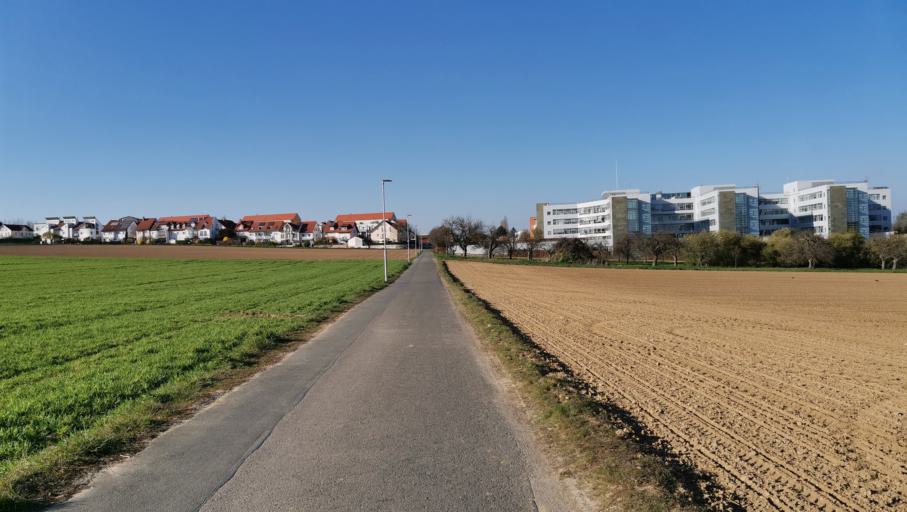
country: DE
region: Hesse
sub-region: Regierungsbezirk Darmstadt
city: Bad Vilbel
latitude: 50.2001
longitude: 8.7411
